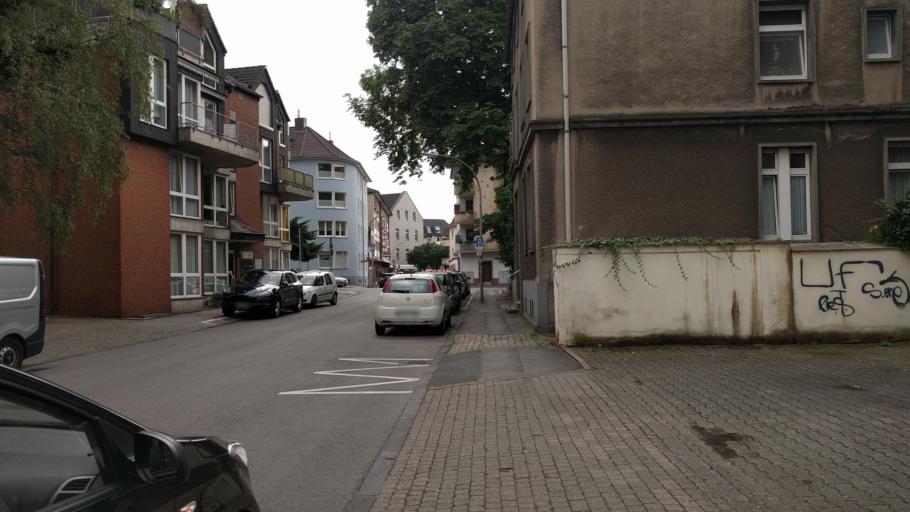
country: DE
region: North Rhine-Westphalia
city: Witten
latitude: 51.4392
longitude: 7.3313
